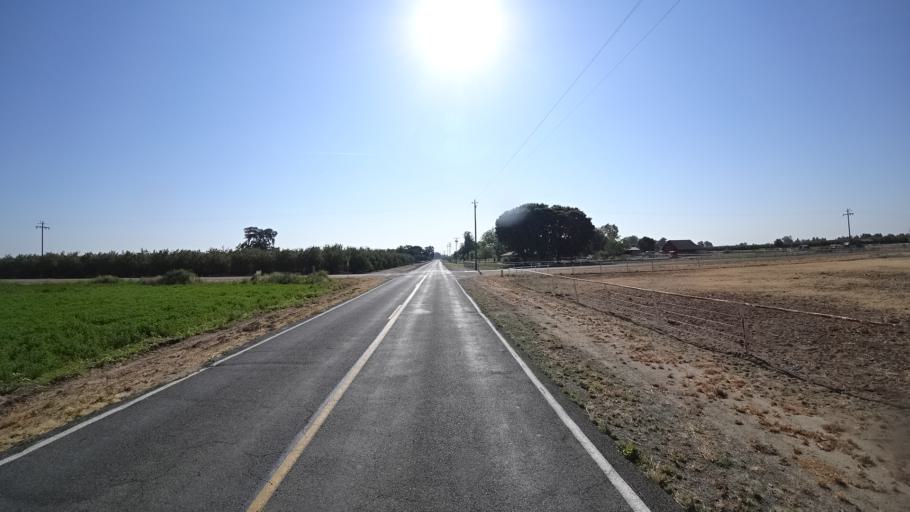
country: US
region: California
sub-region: Fresno County
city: Riverdale
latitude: 36.3657
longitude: -119.8347
